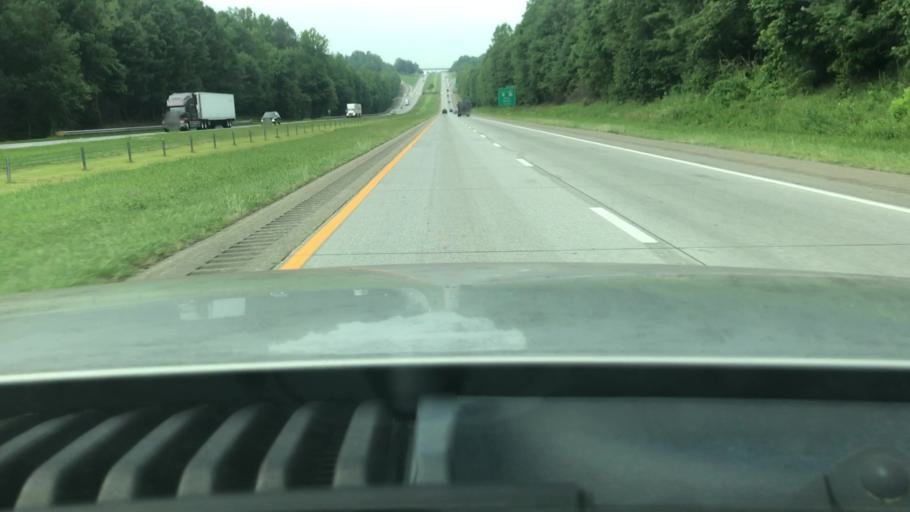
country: US
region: North Carolina
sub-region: Surry County
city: Elkin
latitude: 36.2933
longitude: -80.8144
